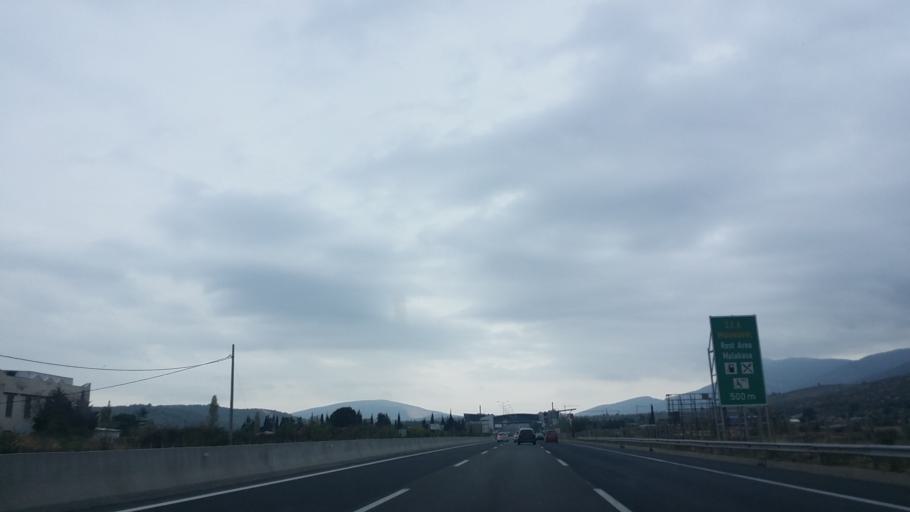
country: GR
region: Attica
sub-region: Nomarchia Anatolikis Attikis
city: Avlonas
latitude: 38.2591
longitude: 23.7390
